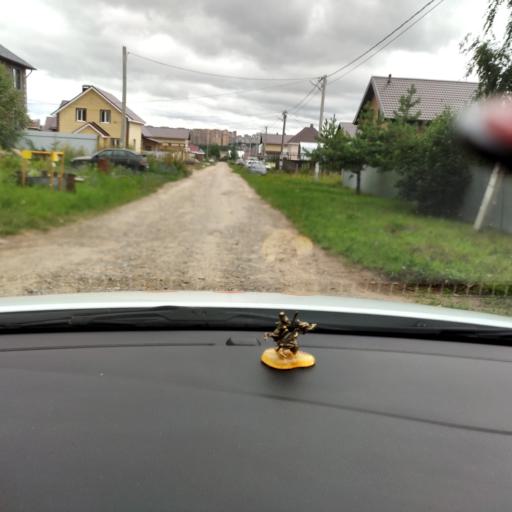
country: RU
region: Tatarstan
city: Vysokaya Gora
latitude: 55.7807
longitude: 49.2698
